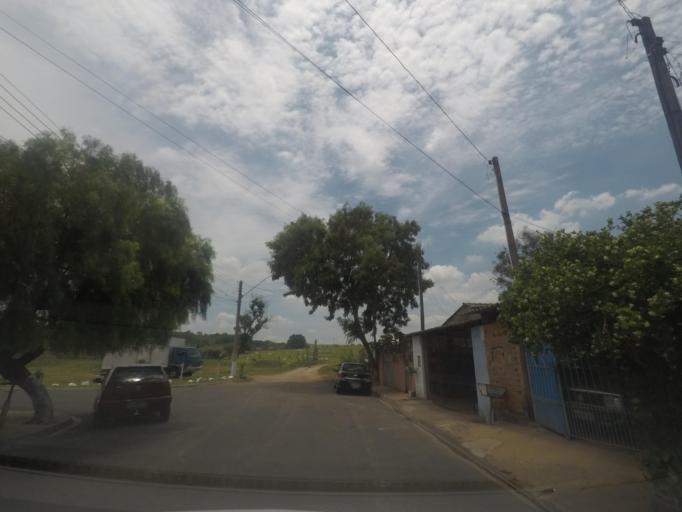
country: BR
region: Sao Paulo
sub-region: Nova Odessa
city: Nova Odessa
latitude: -22.7911
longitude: -47.2756
